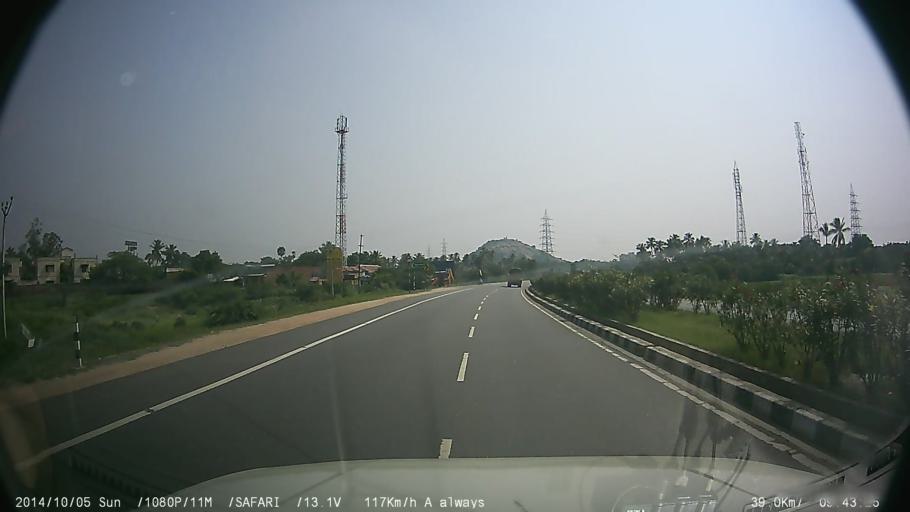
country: IN
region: Tamil Nadu
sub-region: Erode
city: Bhavani
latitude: 11.4499
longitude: 77.7606
